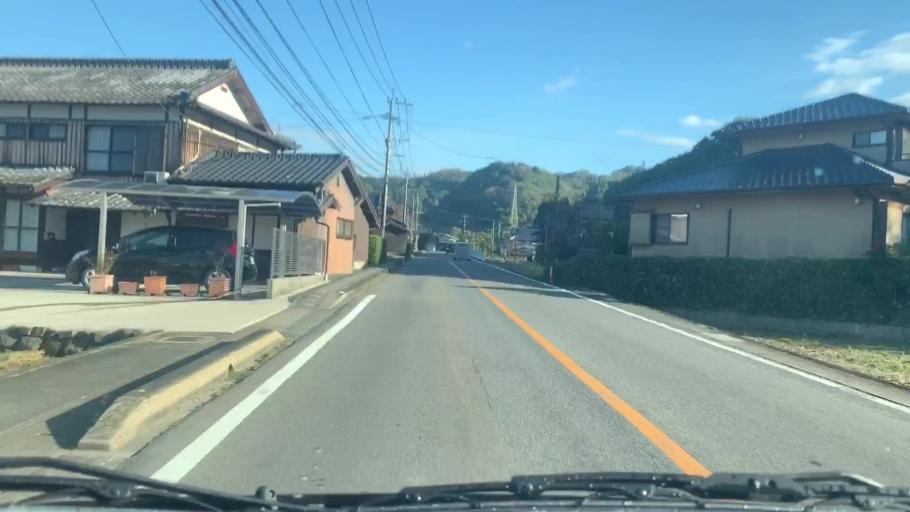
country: JP
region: Saga Prefecture
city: Takeocho-takeo
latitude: 33.2325
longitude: 130.0612
